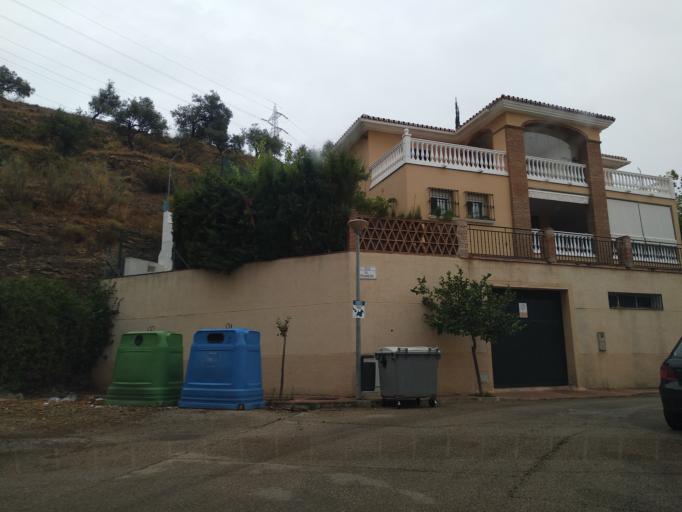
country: ES
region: Andalusia
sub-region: Provincia de Malaga
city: Malaga
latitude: 36.7437
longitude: -4.4746
